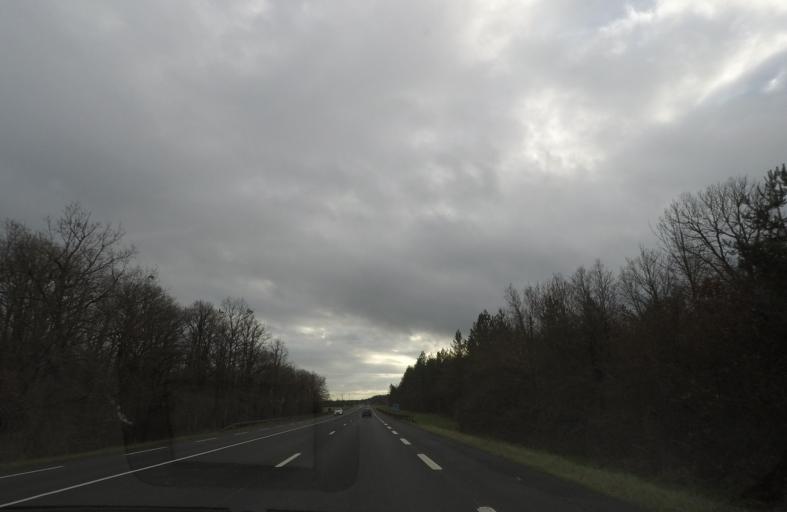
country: FR
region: Centre
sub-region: Departement du Loir-et-Cher
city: Soings-en-Sologne
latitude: 47.4506
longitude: 1.5344
